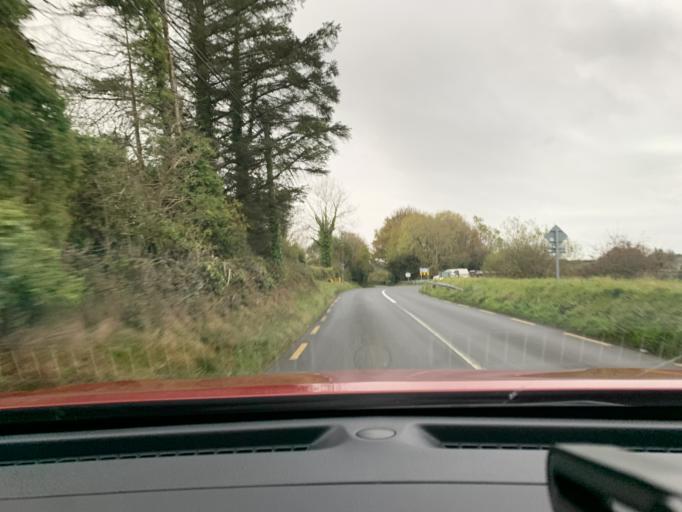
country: IE
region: Connaught
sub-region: Sligo
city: Ballymote
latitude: 54.0639
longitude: -8.5077
